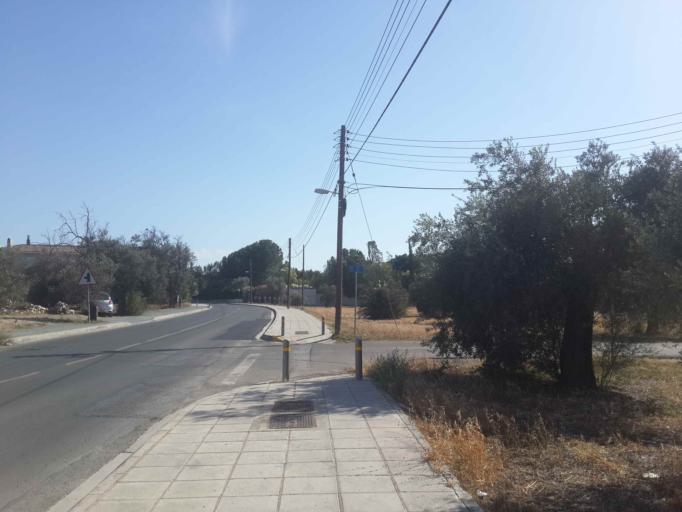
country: CY
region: Lefkosia
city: Nicosia
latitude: 35.1512
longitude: 33.3357
